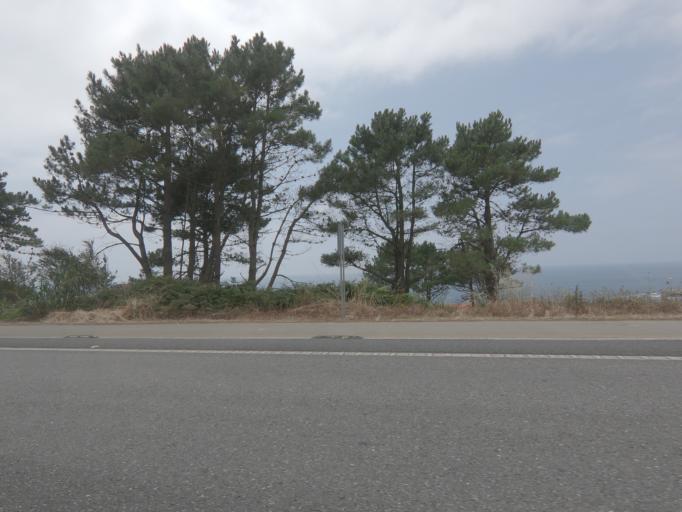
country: ES
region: Galicia
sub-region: Provincia de Pontevedra
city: Oia
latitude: 41.9688
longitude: -8.8838
